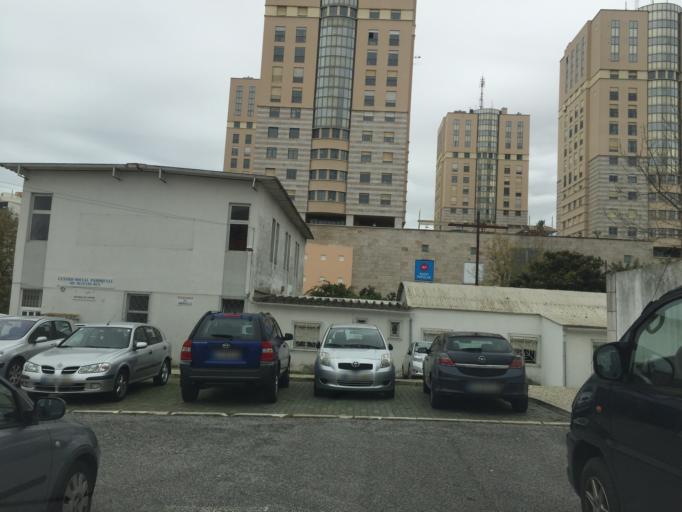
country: PT
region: Lisbon
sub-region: Loures
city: Moscavide
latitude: 38.7633
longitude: -9.1133
